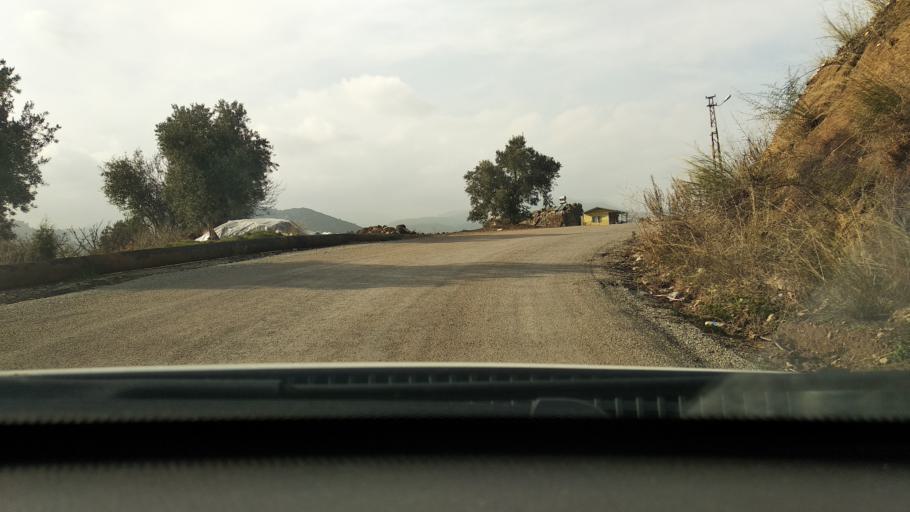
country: TR
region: Mersin
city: Kuzucubelen
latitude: 36.8699
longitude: 34.4691
